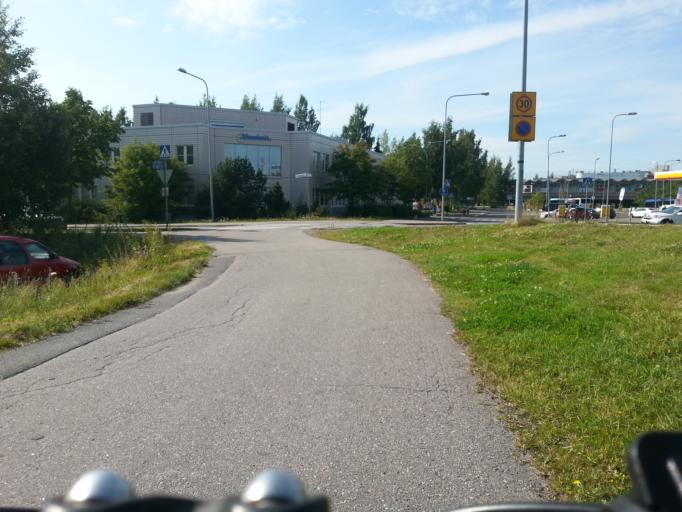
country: FI
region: Uusimaa
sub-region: Helsinki
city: Vantaa
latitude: 60.2406
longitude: 24.9960
